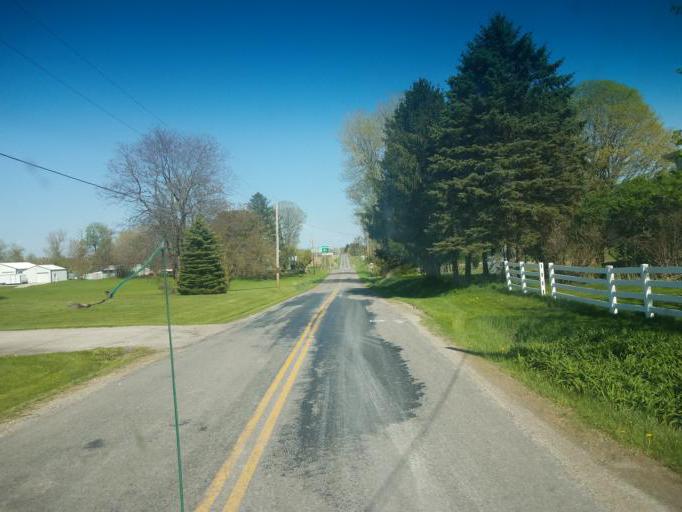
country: US
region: Ohio
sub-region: Medina County
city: Lodi
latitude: 40.9959
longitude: -81.9842
